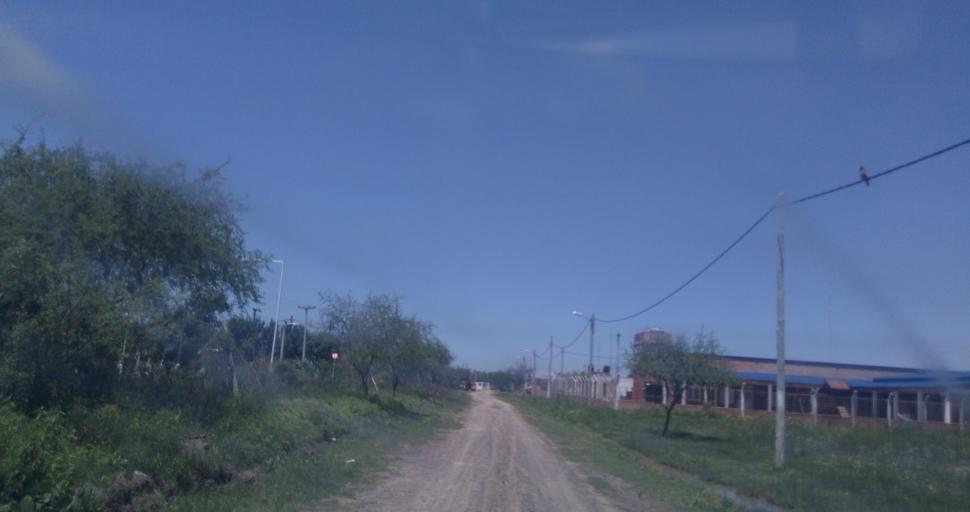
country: AR
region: Chaco
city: Resistencia
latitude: -27.4793
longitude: -59.0124
